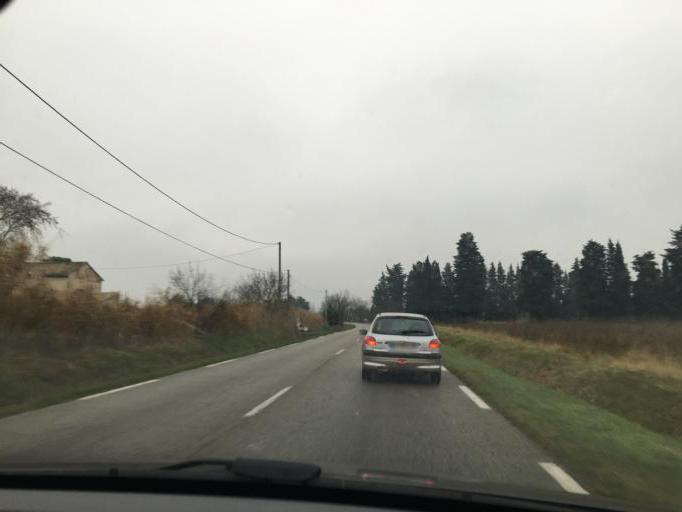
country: FR
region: Provence-Alpes-Cote d'Azur
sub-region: Departement du Vaucluse
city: Lagnes
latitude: 43.9044
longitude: 5.0821
